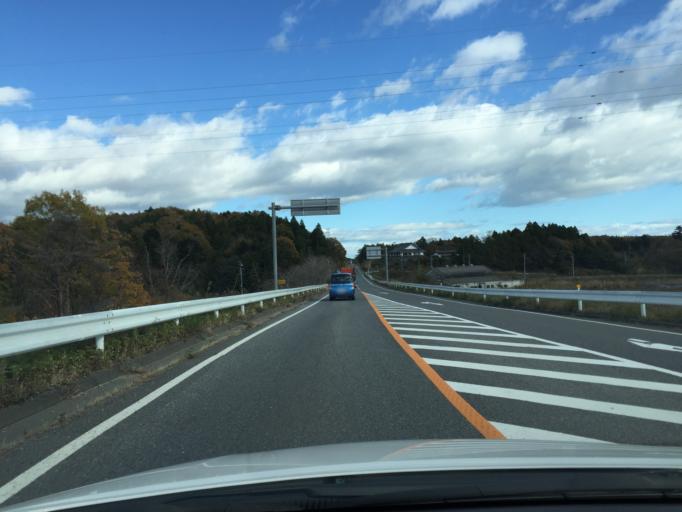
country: JP
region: Fukushima
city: Namie
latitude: 37.4161
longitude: 140.9993
